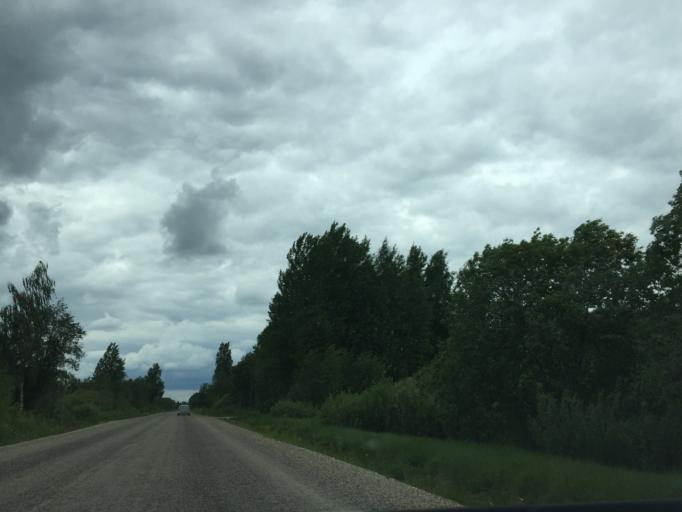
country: LV
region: Dagda
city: Dagda
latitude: 56.0574
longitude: 27.5670
